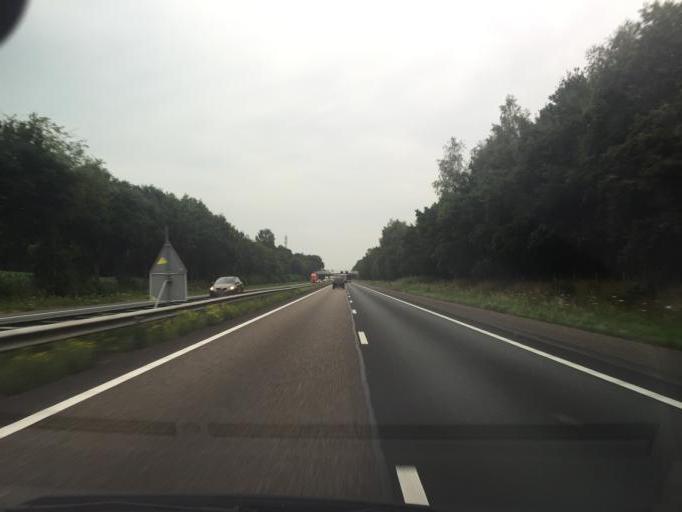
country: NL
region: North Brabant
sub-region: Gemeente Geldrop-Mierlo
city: Geldrop
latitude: 51.4105
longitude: 5.5739
